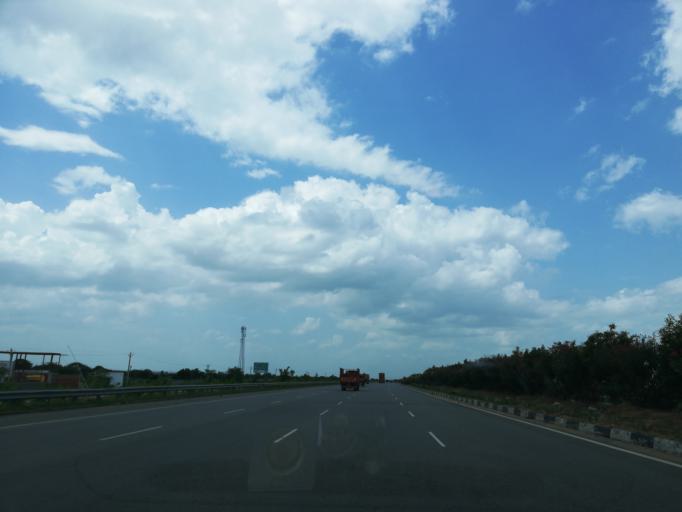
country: IN
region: Telangana
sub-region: Medak
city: Patancheru
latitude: 17.4855
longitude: 78.2459
